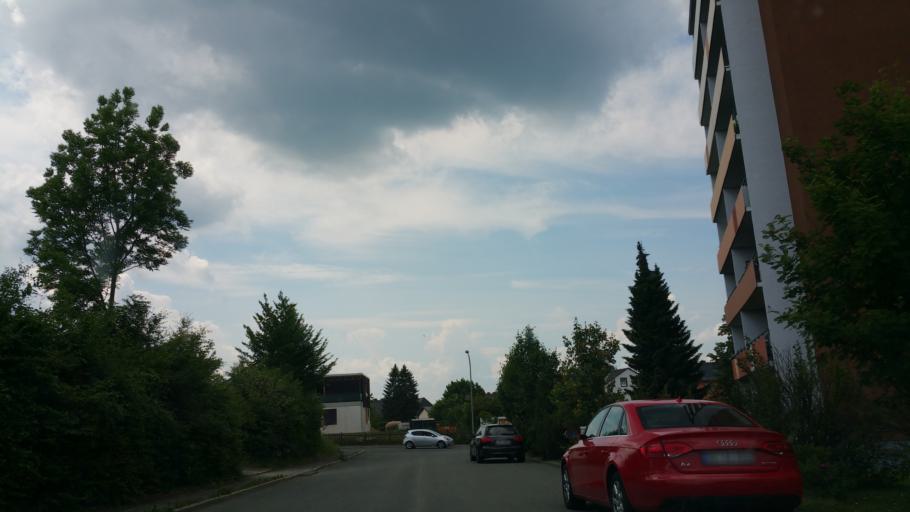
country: DE
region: Bavaria
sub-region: Upper Franconia
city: Schwarzenbach an der Saale
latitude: 50.2209
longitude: 11.9477
